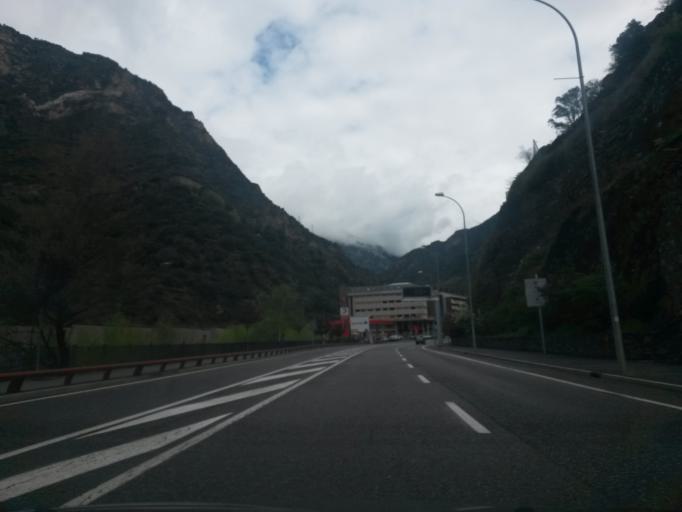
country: AD
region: Sant Julia de Loria
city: Sant Julia de Loria
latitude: 42.4560
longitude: 1.4865
